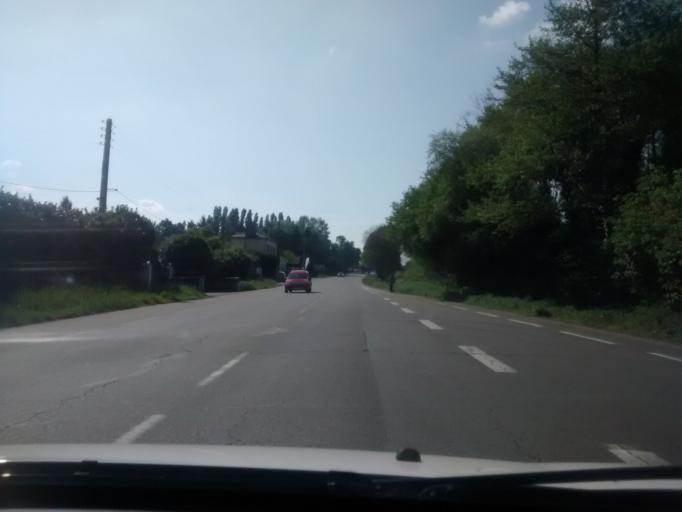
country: FR
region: Brittany
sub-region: Departement d'Ille-et-Vilaine
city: Montgermont
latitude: 48.1514
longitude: -1.7054
